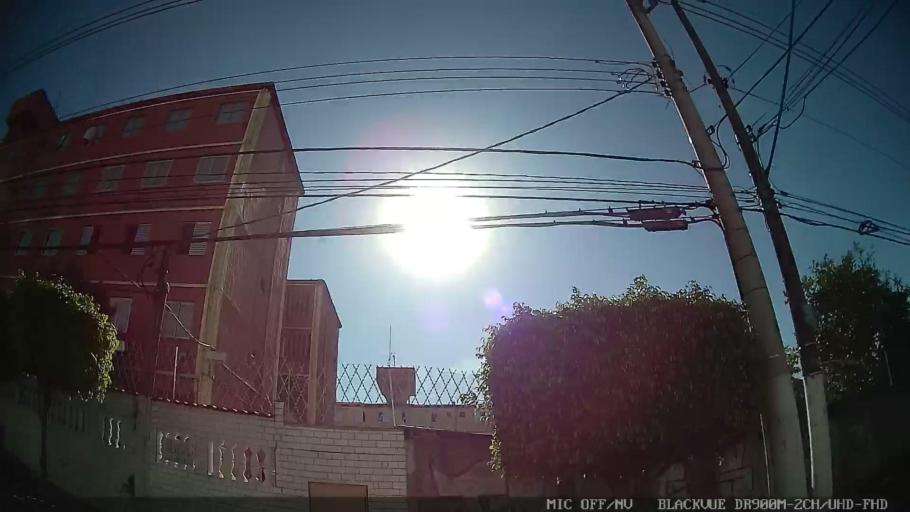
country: BR
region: Sao Paulo
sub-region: Guarulhos
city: Guarulhos
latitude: -23.5481
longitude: -46.4845
